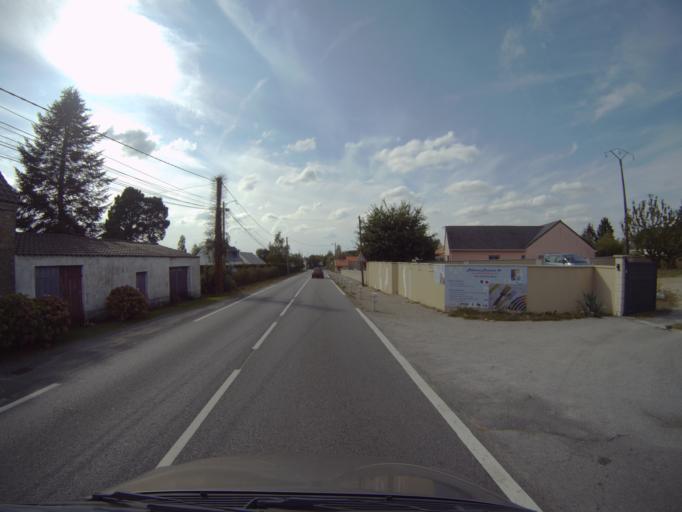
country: FR
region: Pays de la Loire
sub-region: Departement de la Loire-Atlantique
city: Sautron
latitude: 47.2448
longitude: -1.6892
